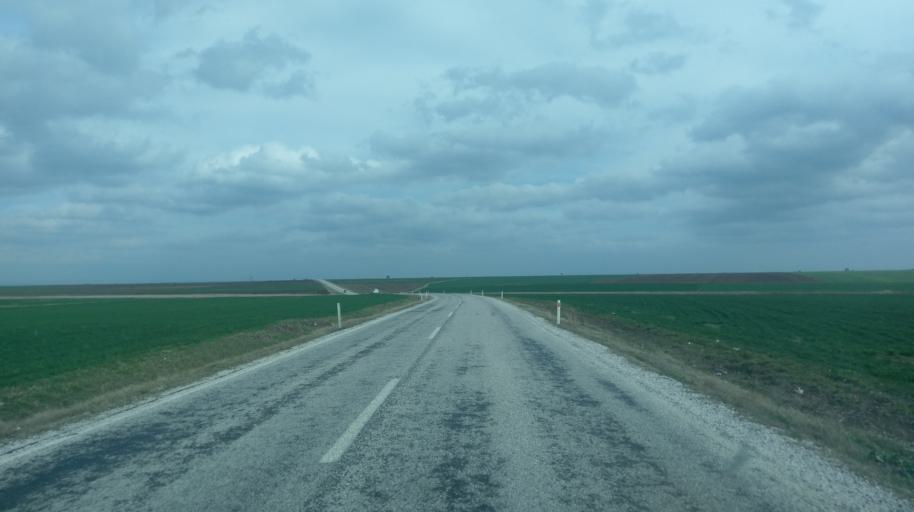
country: TR
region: Edirne
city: Haskoy
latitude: 41.6497
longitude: 26.8853
